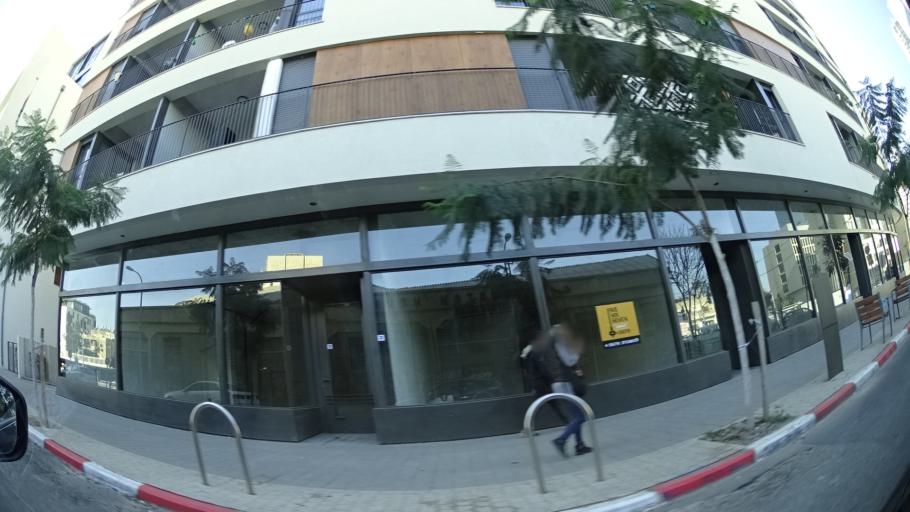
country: IL
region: Tel Aviv
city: Tel Aviv
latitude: 32.0635
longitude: 34.7768
